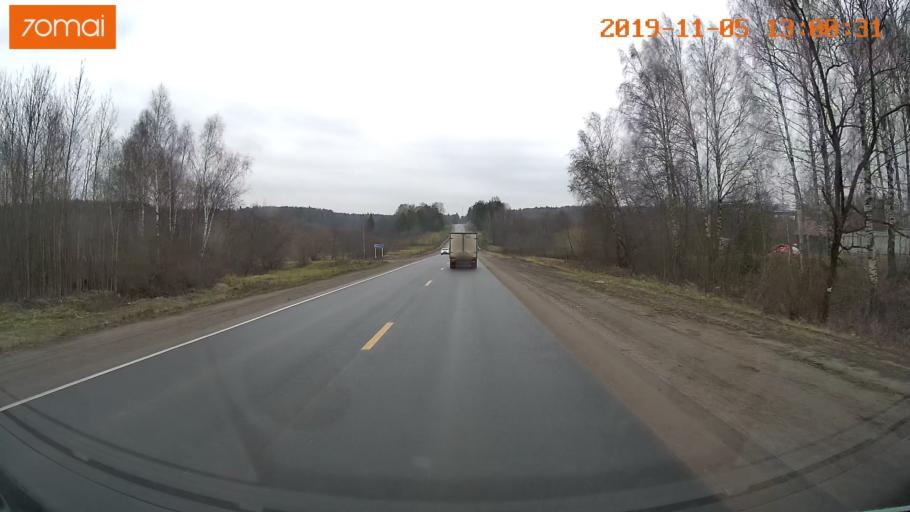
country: RU
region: Ivanovo
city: Kokhma
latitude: 56.9136
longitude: 41.1463
